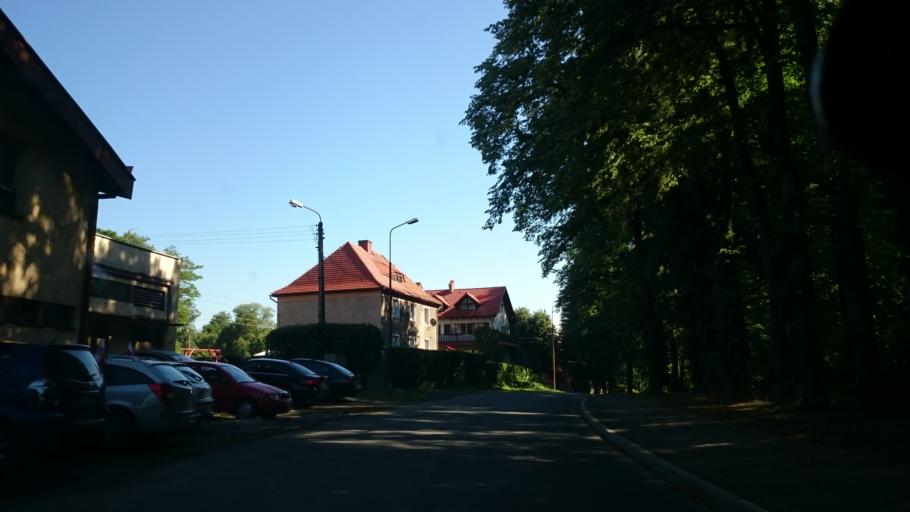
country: PL
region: Lower Silesian Voivodeship
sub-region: Powiat klodzki
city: Bystrzyca Klodzka
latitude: 50.2904
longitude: 16.6451
